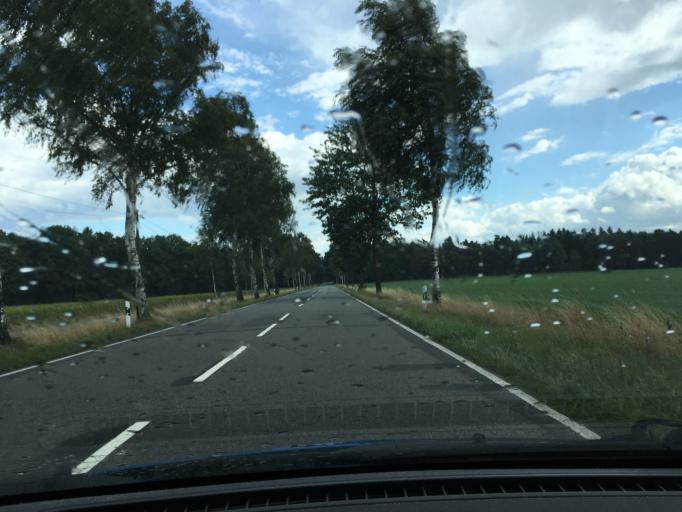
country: DE
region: Lower Saxony
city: Wietzendorf
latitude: 52.9834
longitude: 9.9405
